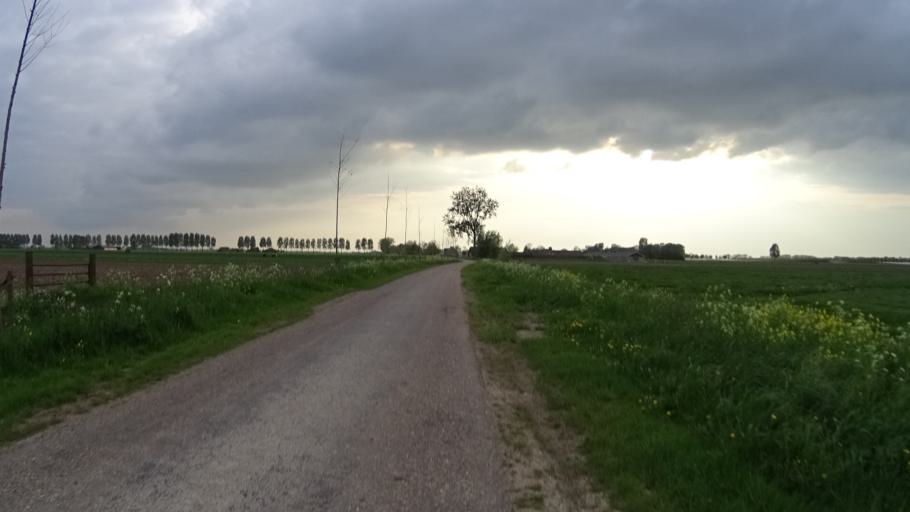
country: NL
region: North Brabant
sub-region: Gemeente Aalburg
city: Aalburg
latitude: 51.7652
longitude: 5.0879
